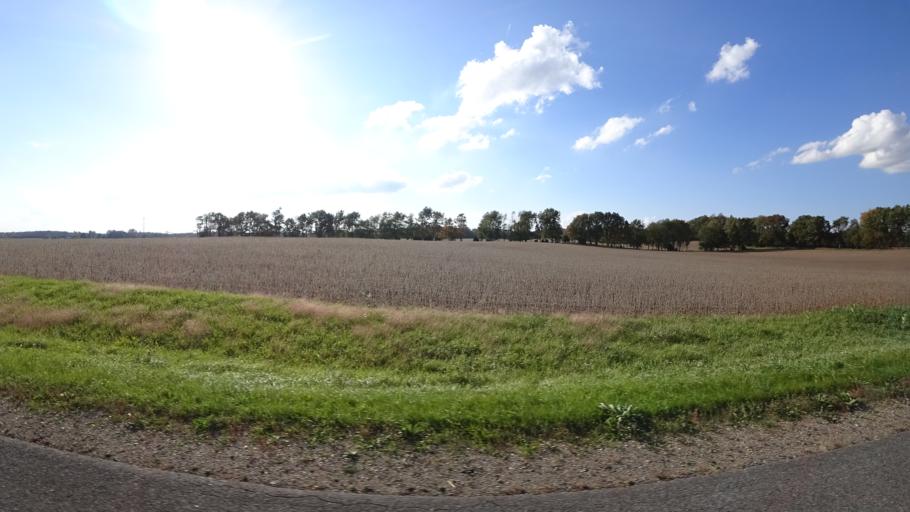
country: US
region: Michigan
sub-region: Saint Joseph County
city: Centreville
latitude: 41.8988
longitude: -85.5066
